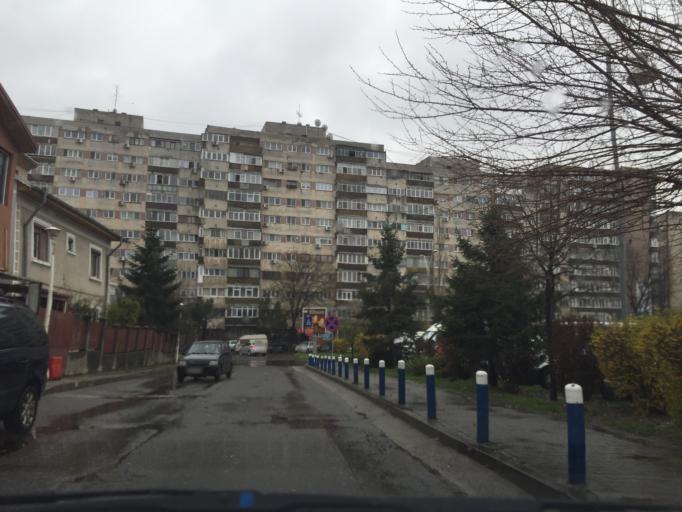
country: RO
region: Ilfov
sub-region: Comuna Chiajna
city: Rosu
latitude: 44.4283
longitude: 26.0367
